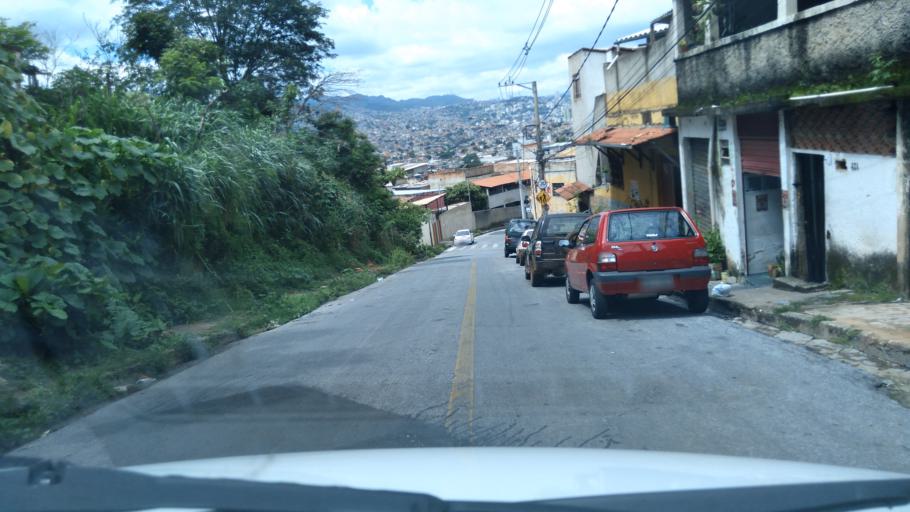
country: BR
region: Minas Gerais
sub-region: Belo Horizonte
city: Belo Horizonte
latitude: -19.8965
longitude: -43.8928
